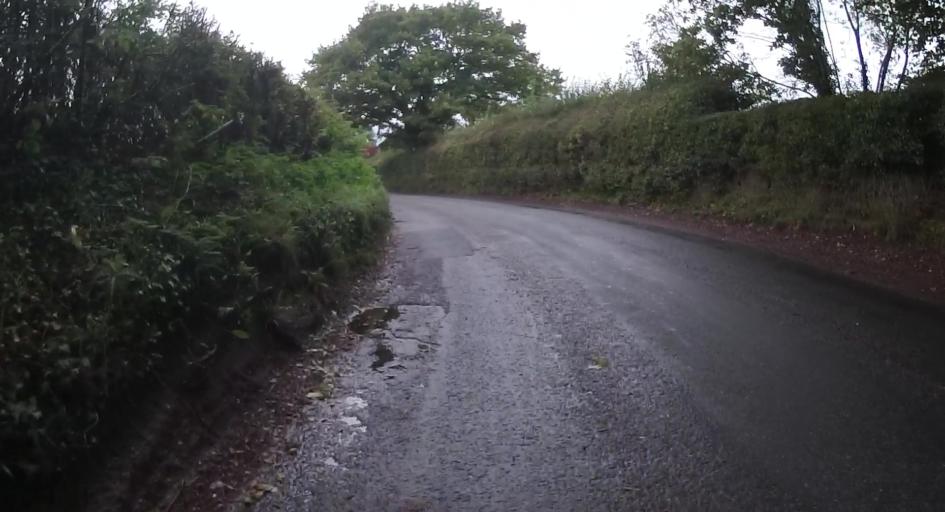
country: GB
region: England
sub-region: Hampshire
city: Tadley
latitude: 51.4104
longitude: -1.1735
